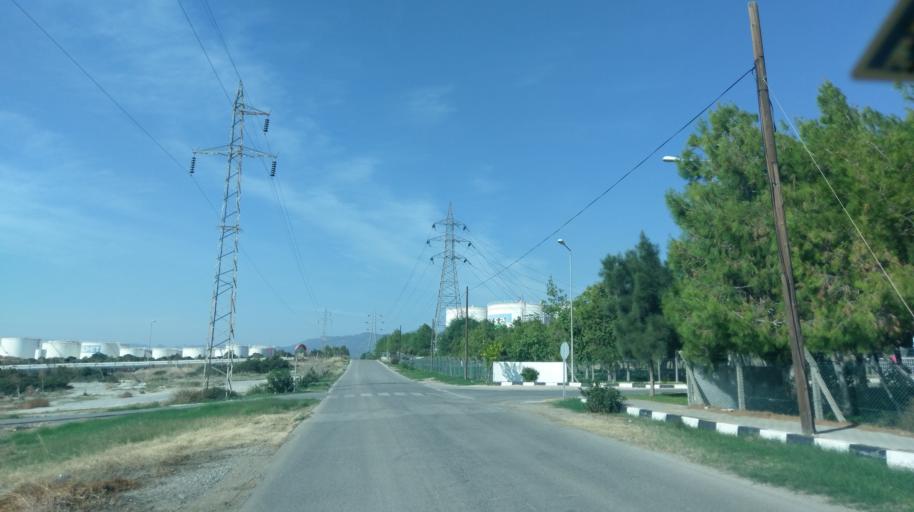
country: CY
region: Ammochostos
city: Trikomo
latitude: 35.3282
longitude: 33.9988
